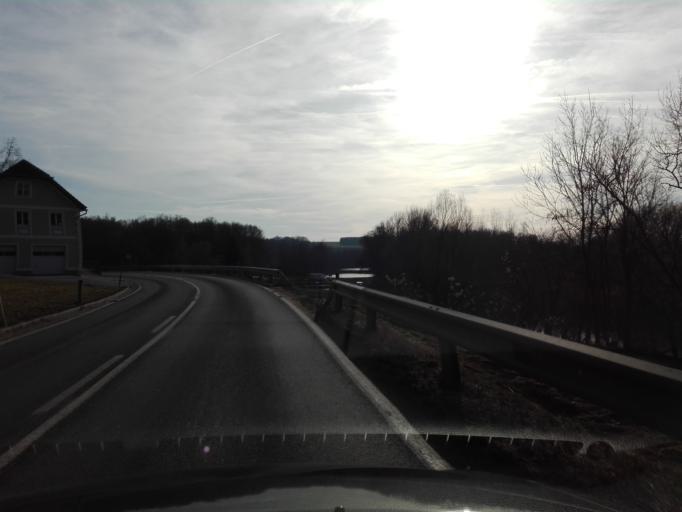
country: AT
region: Lower Austria
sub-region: Politischer Bezirk Amstetten
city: Amstetten
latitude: 48.1948
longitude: 14.8476
